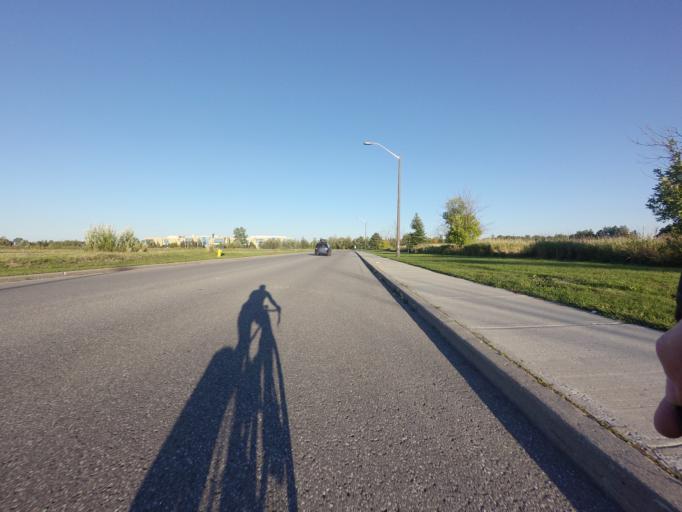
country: CA
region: Ontario
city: Ottawa
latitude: 45.2948
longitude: -75.7106
